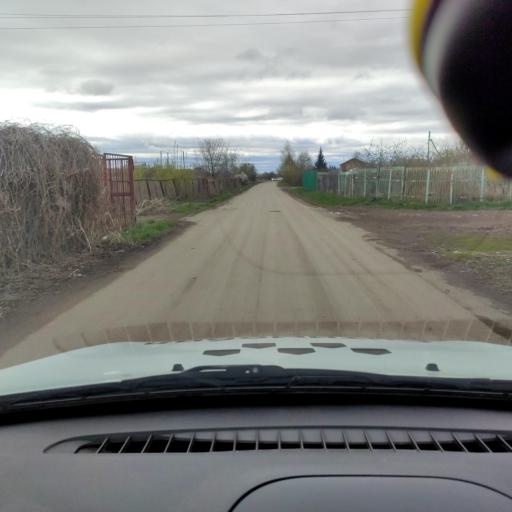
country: RU
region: Samara
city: Tol'yatti
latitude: 53.5814
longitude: 49.3184
